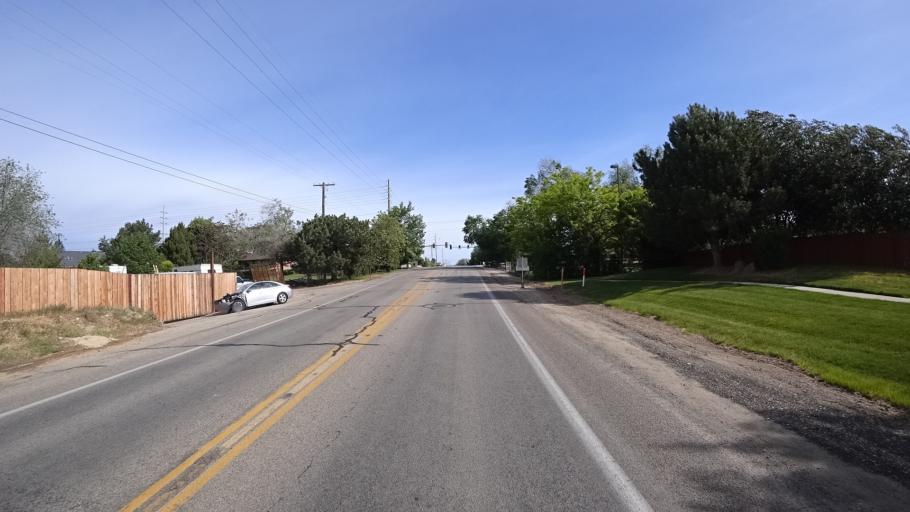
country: US
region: Idaho
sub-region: Ada County
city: Meridian
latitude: 43.5600
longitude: -116.3344
